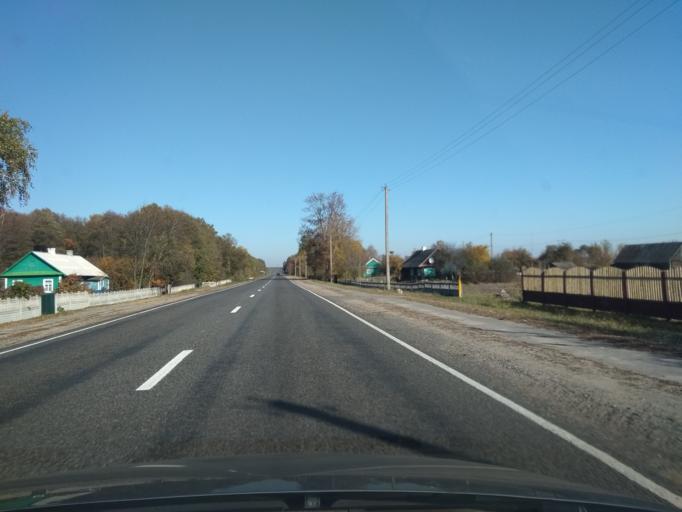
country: BY
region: Brest
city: Malaryta
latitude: 51.9880
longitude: 24.2070
